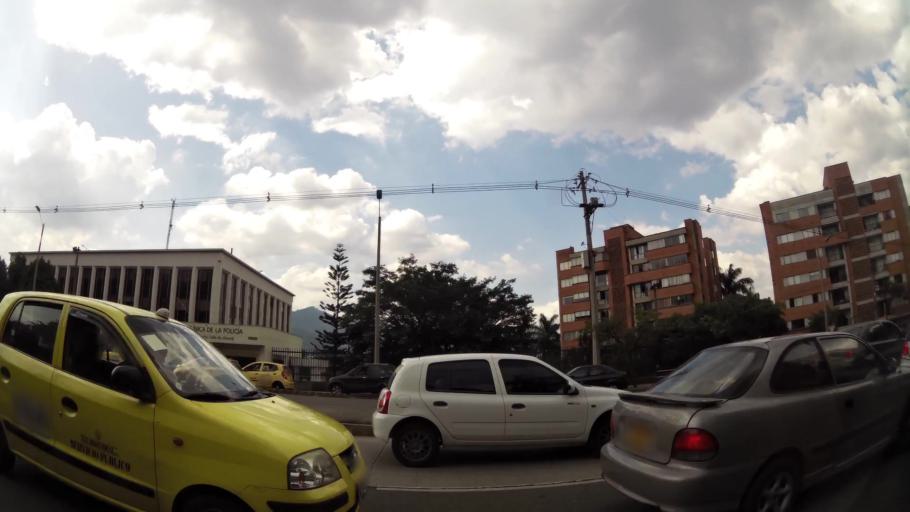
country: CO
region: Antioquia
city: Envigado
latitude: 6.1620
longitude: -75.5979
